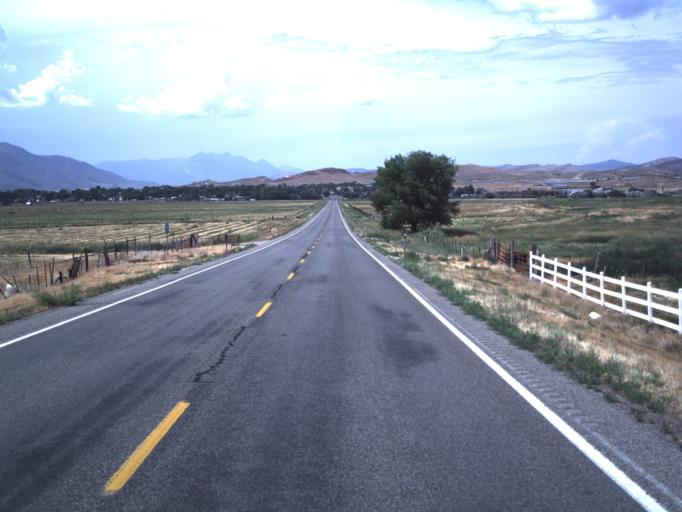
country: US
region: Utah
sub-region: Sanpete County
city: Moroni
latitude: 39.5084
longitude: -111.5692
